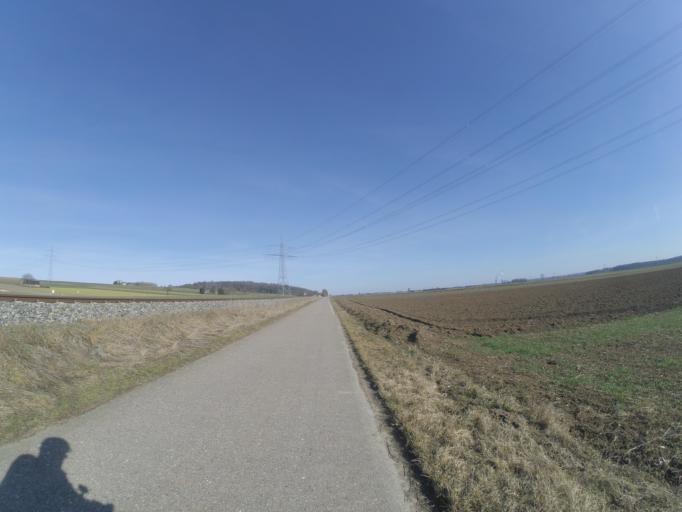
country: DE
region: Baden-Wuerttemberg
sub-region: Regierungsbezirk Stuttgart
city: Niederstotzingen
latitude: 48.5377
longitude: 10.2466
